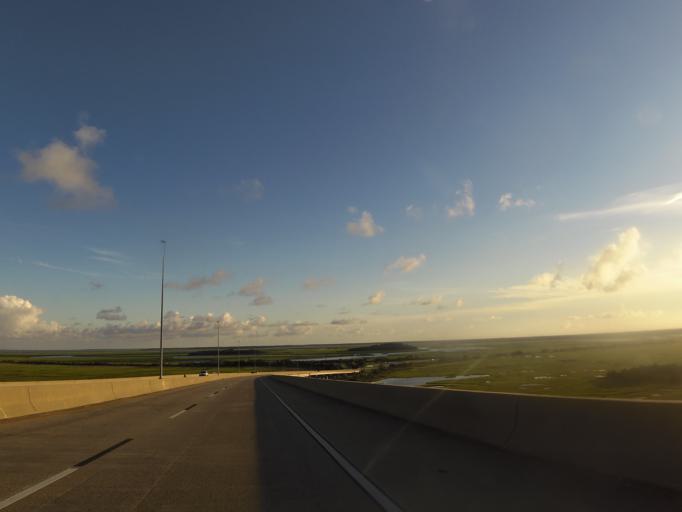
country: US
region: Georgia
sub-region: Glynn County
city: Brunswick
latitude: 31.1120
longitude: -81.4872
